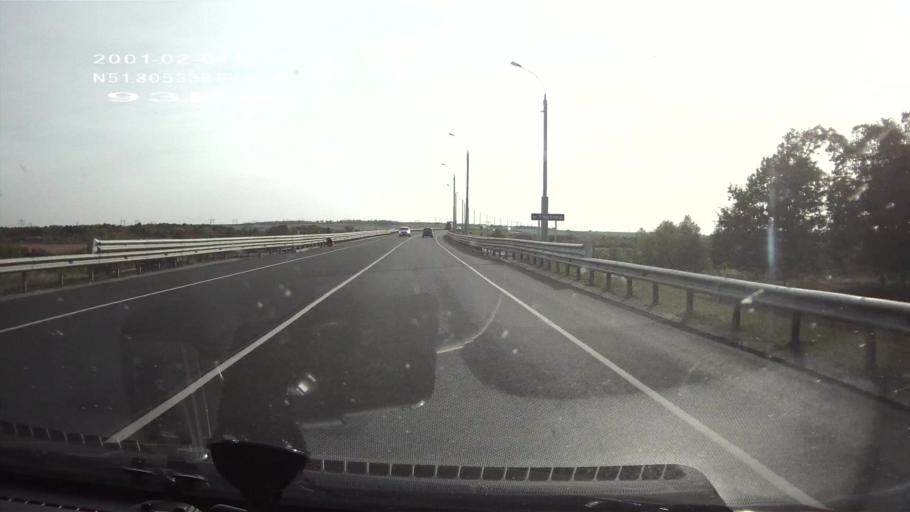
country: RU
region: Saratov
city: Yelshanka
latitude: 51.8048
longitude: 46.1923
